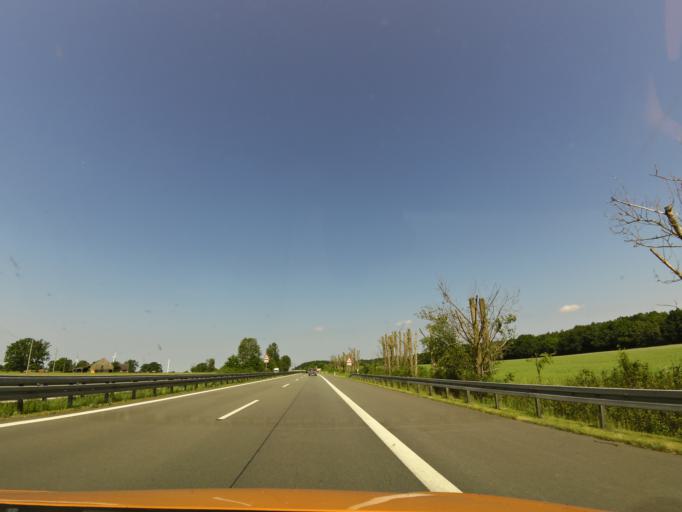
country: DE
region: Brandenburg
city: Gerdshagen
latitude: 53.2514
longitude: 12.1724
